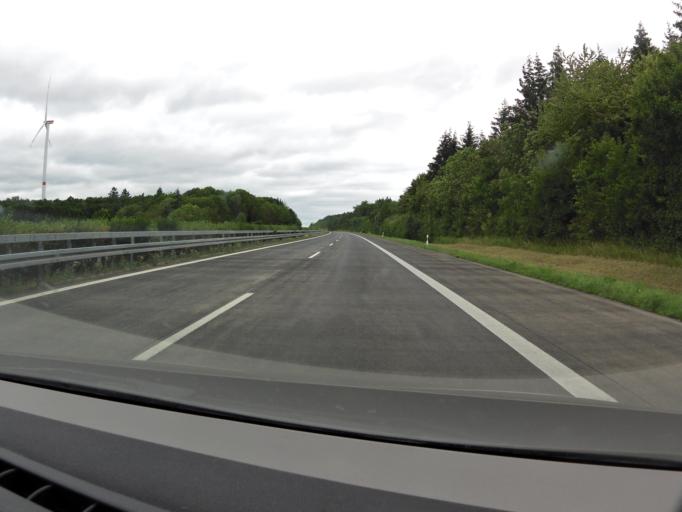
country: DE
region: Baden-Wuerttemberg
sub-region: Regierungsbezirk Stuttgart
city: Buch am Ahorn
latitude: 49.4836
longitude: 9.5655
